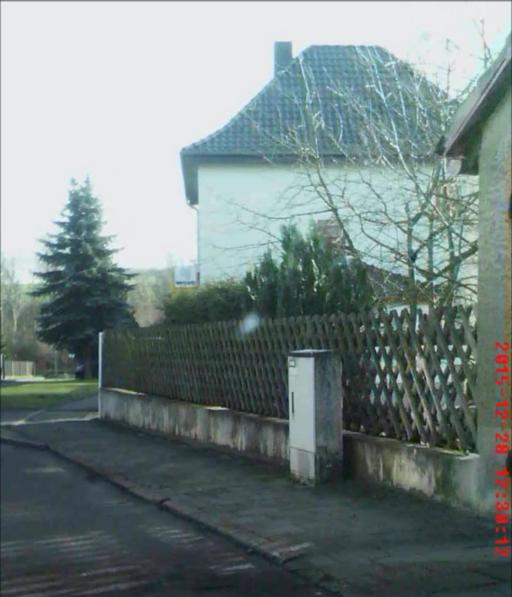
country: DE
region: Thuringia
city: Ossmanstedt
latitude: 51.0207
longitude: 11.4362
